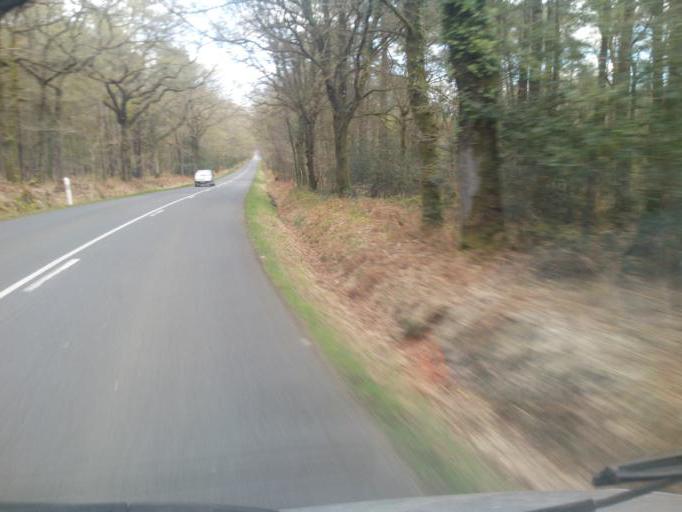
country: FR
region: Brittany
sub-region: Departement d'Ille-et-Vilaine
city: Paimpont
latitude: 48.0138
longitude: -2.1379
